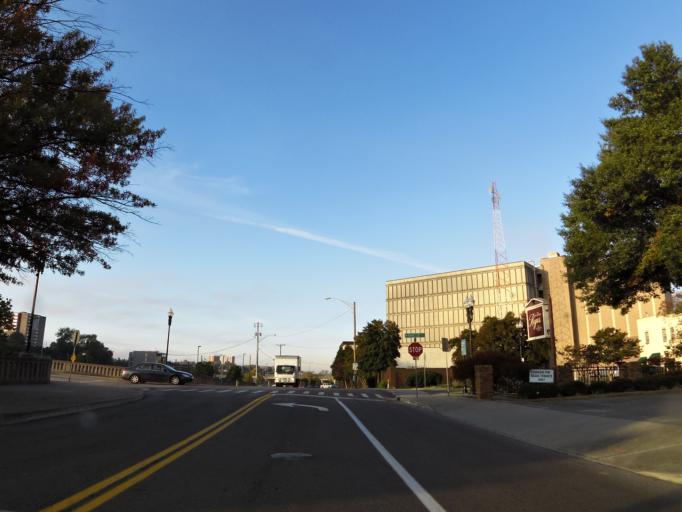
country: US
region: Tennessee
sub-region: Knox County
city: Knoxville
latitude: 35.9703
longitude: -83.9218
